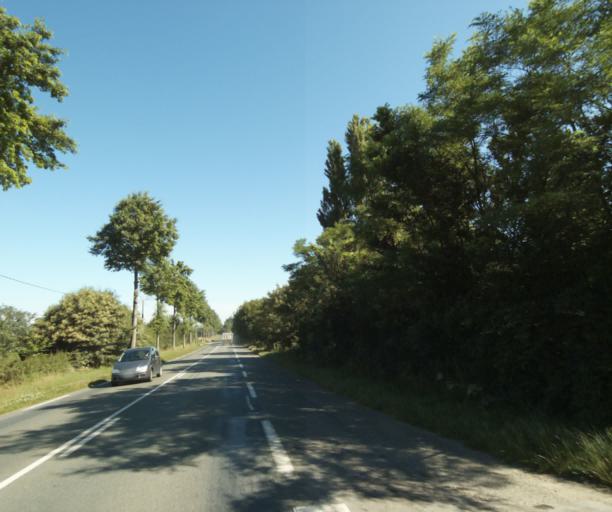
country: FR
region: Pays de la Loire
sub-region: Departement de la Mayenne
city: Laval
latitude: 48.0410
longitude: -0.7419
